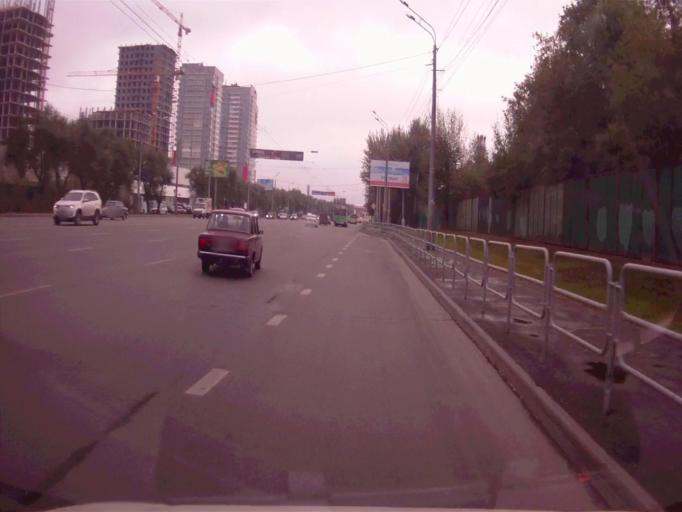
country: RU
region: Chelyabinsk
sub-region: Gorod Chelyabinsk
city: Chelyabinsk
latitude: 55.1710
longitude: 61.3679
